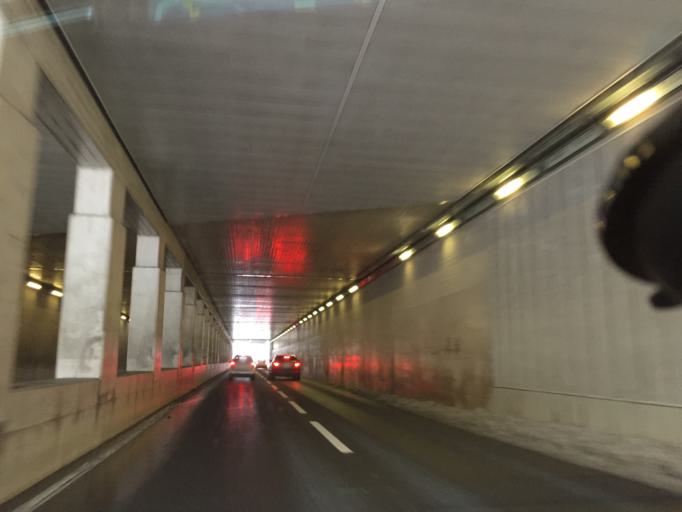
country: CH
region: Schwyz
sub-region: Bezirk Hoefe
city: Schindellegi
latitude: 47.1741
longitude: 8.7124
